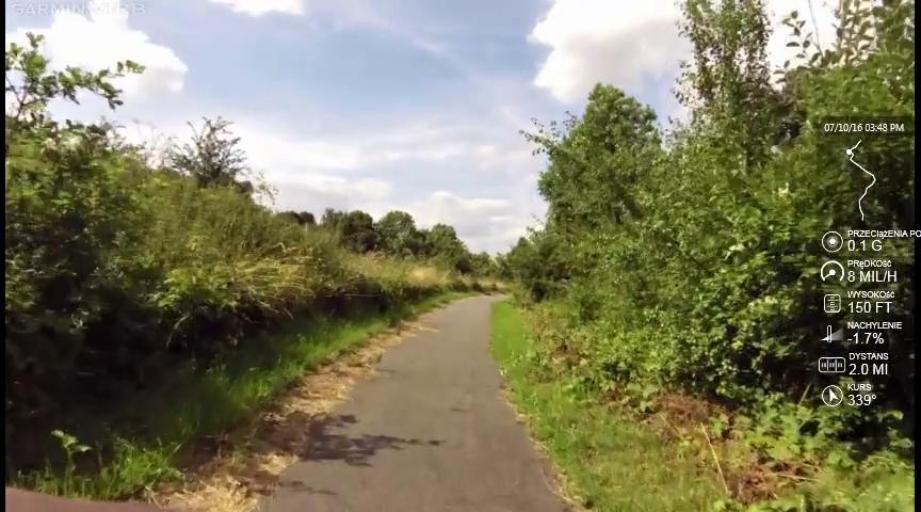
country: PL
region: West Pomeranian Voivodeship
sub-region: Powiat gryfinski
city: Banie
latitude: 53.1374
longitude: 14.6120
